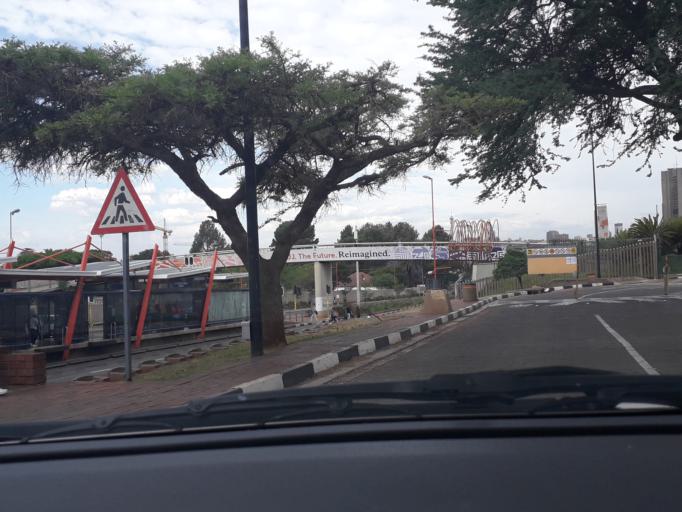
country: ZA
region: Gauteng
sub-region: City of Johannesburg Metropolitan Municipality
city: Johannesburg
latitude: -26.1822
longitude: 27.9986
